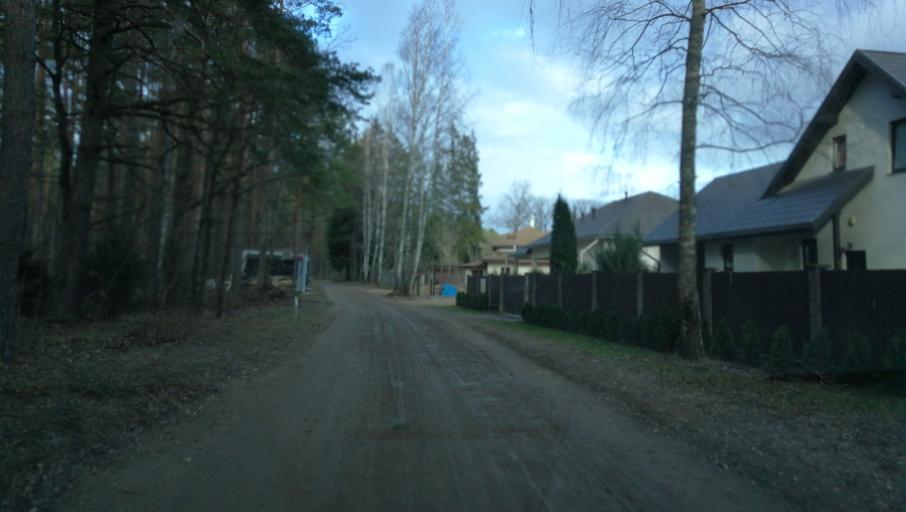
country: LV
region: Adazi
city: Adazi
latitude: 57.0654
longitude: 24.2645
